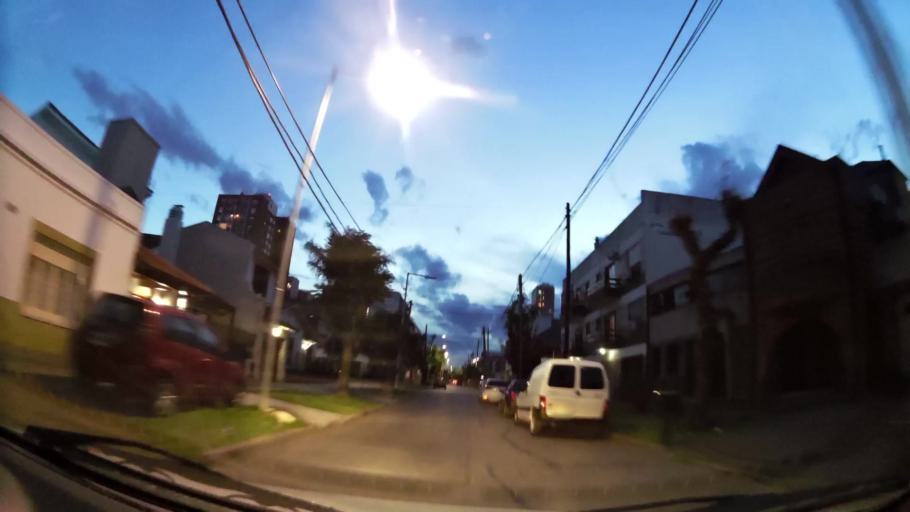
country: AR
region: Buenos Aires
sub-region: Partido de Avellaneda
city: Avellaneda
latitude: -34.6979
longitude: -58.3225
